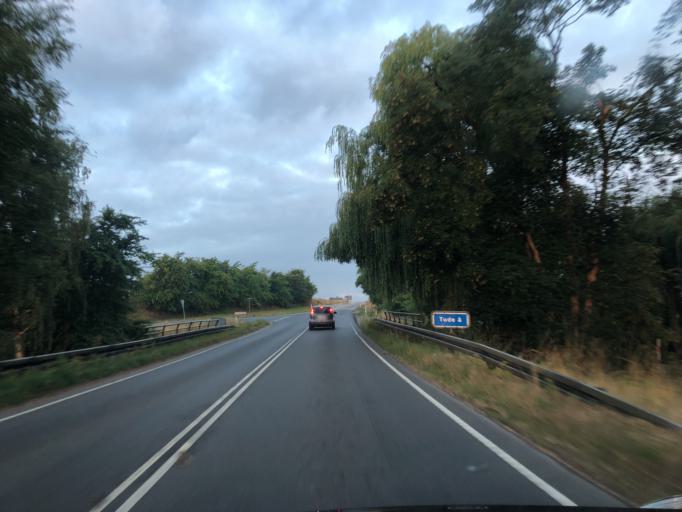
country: DK
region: Zealand
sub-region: Soro Kommune
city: Dianalund
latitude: 55.4909
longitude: 11.5109
